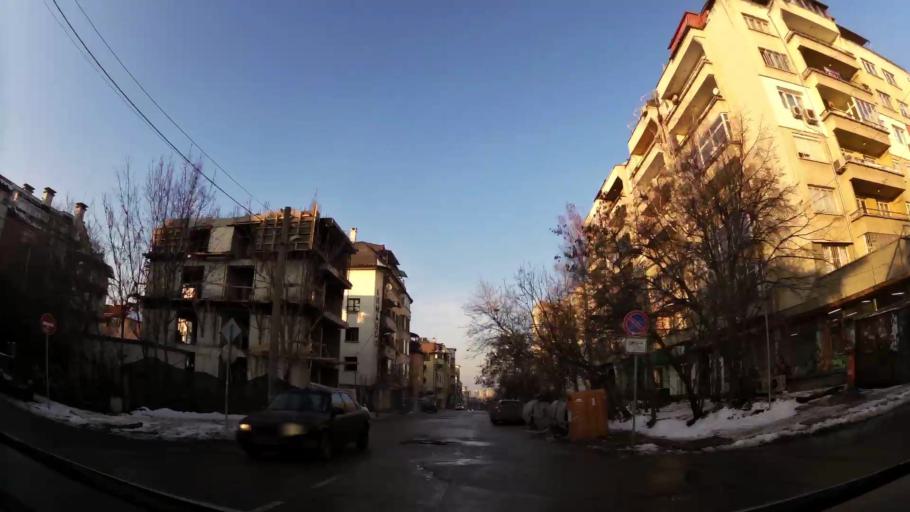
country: BG
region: Sofia-Capital
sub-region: Stolichna Obshtina
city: Sofia
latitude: 42.6928
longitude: 23.3596
